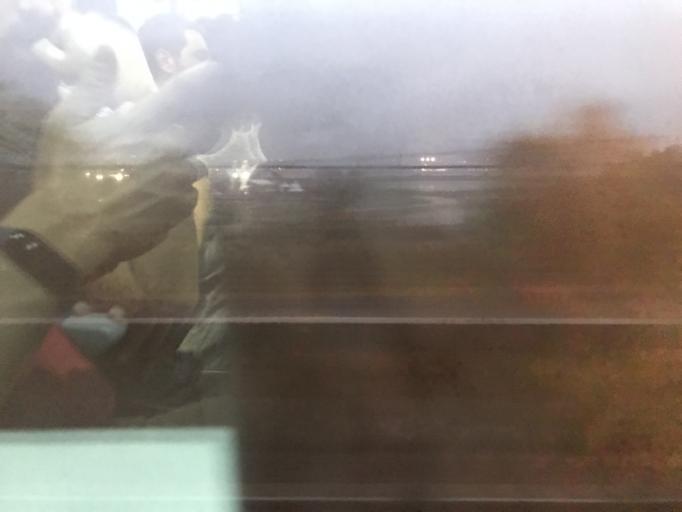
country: TR
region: Kocaeli
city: Korfez
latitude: 40.7473
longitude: 29.7839
